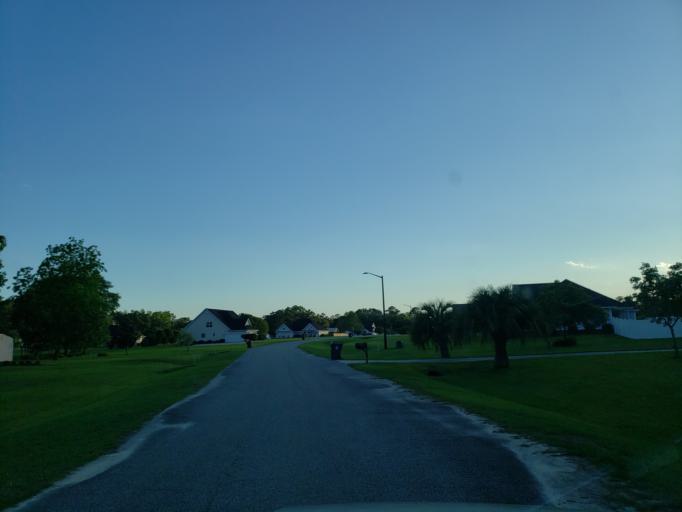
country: US
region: Georgia
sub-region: Lowndes County
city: Valdosta
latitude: 30.7588
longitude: -83.2554
